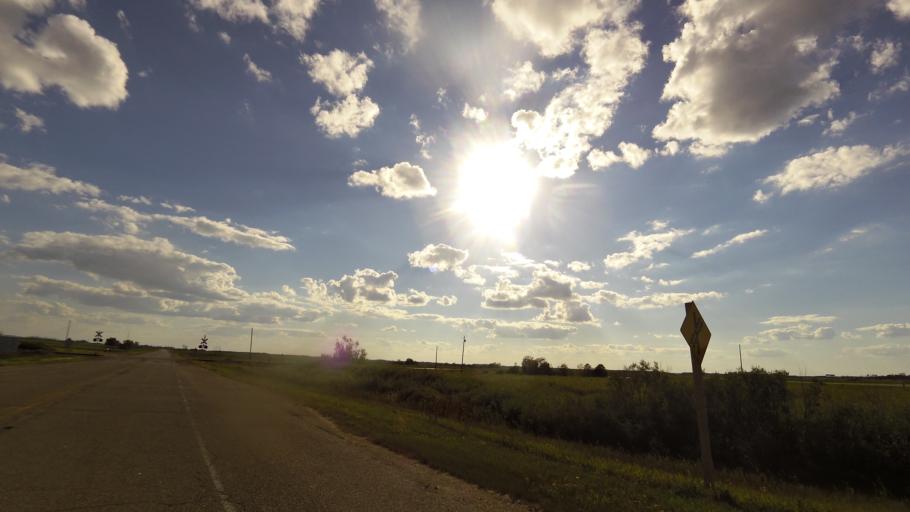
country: CA
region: Saskatchewan
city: Lanigan
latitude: 51.8752
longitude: -105.1920
